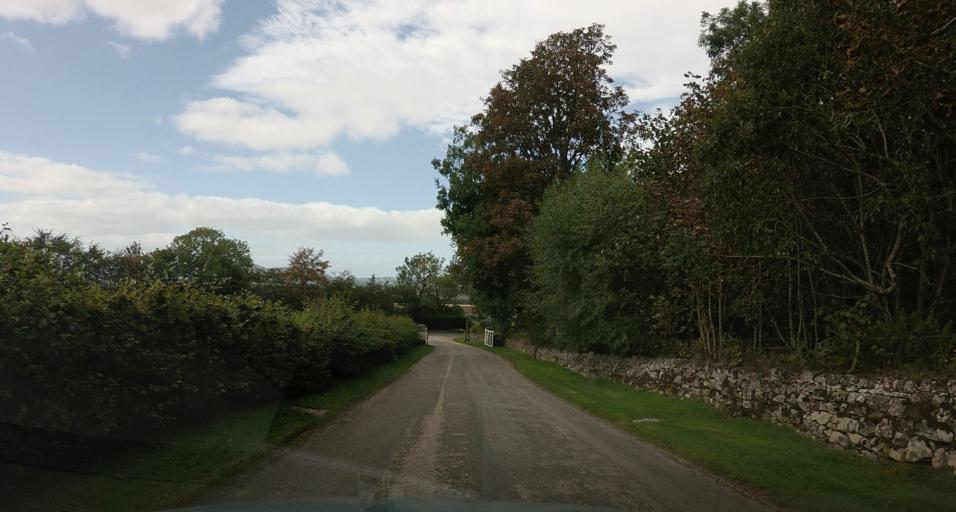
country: GB
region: Scotland
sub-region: Aberdeenshire
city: Kemnay
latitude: 57.2076
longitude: -2.4673
